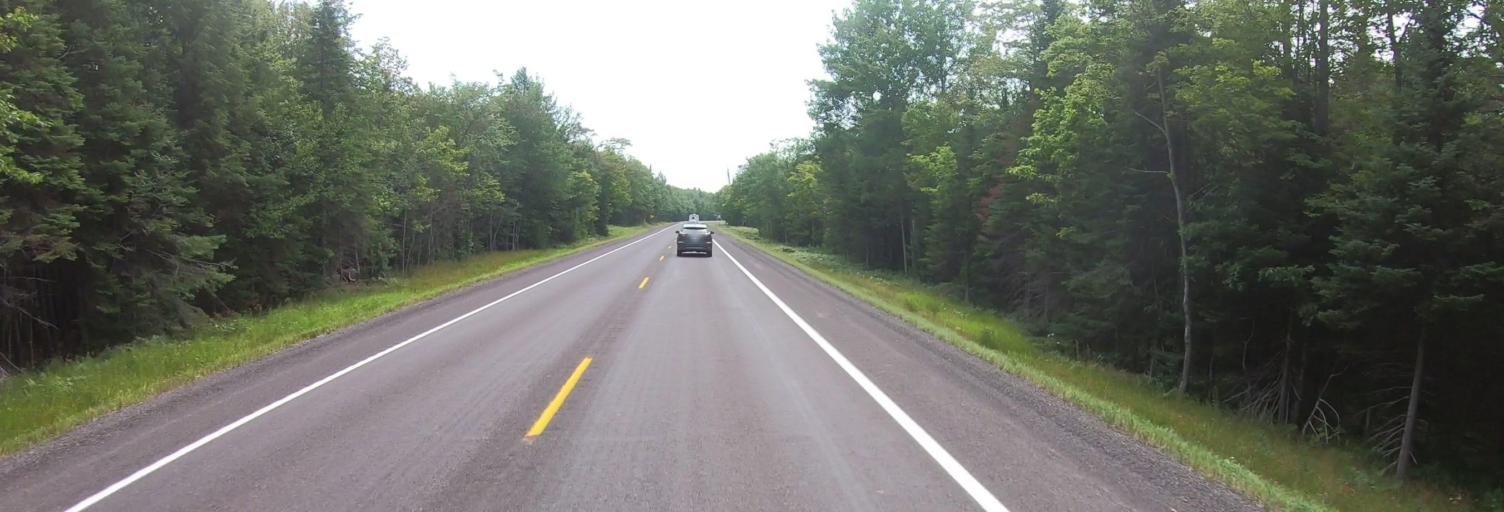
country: US
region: Michigan
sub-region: Houghton County
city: Hancock
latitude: 46.9182
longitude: -88.8171
